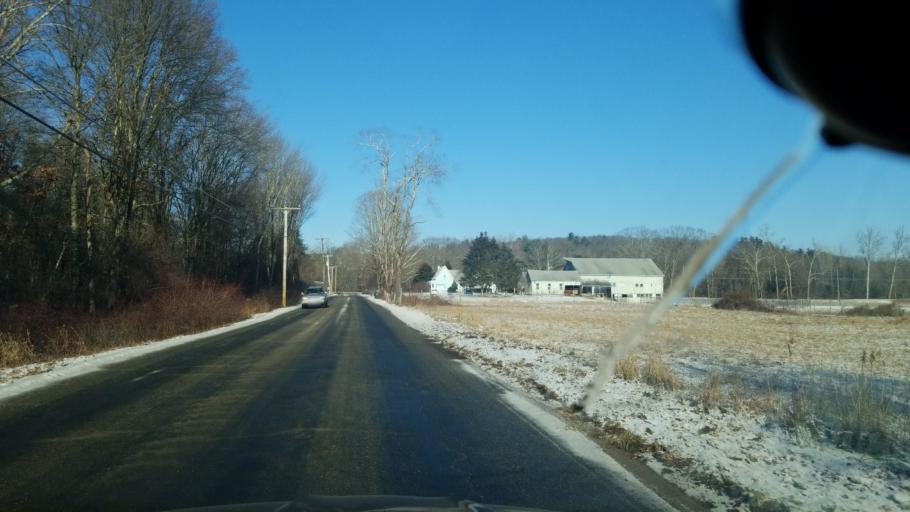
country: US
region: Connecticut
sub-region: Windham County
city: East Brooklyn
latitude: 41.8455
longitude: -71.9334
